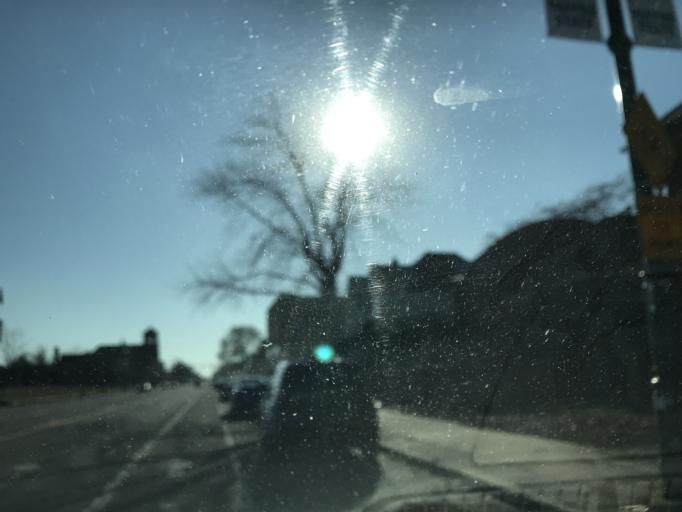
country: US
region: Michigan
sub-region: Wayne County
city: Detroit
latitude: 42.3540
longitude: -83.0796
